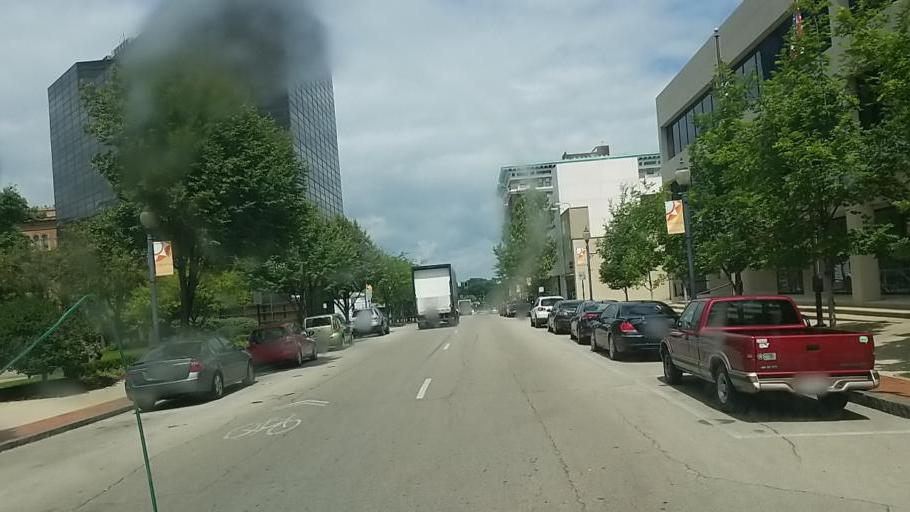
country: US
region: Ohio
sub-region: Clark County
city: Springfield
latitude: 39.9232
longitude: -83.8086
